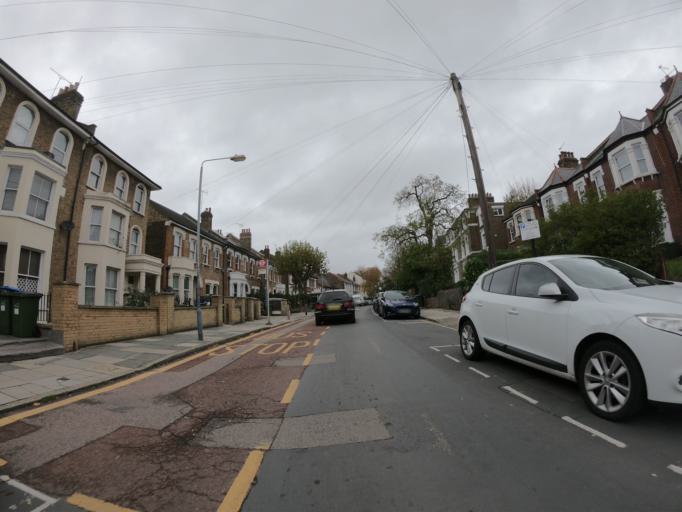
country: GB
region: England
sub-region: Greater London
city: Blackheath
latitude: 51.4845
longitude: 0.0314
